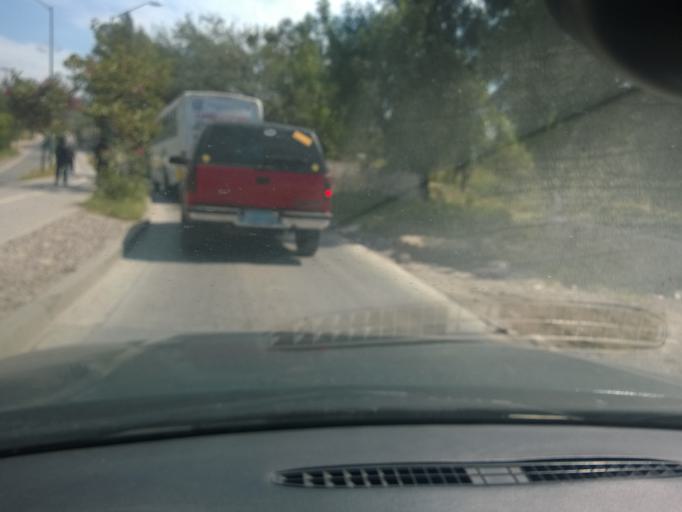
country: MX
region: Guanajuato
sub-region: Leon
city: Ejido la Joya
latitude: 21.1396
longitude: -101.7431
